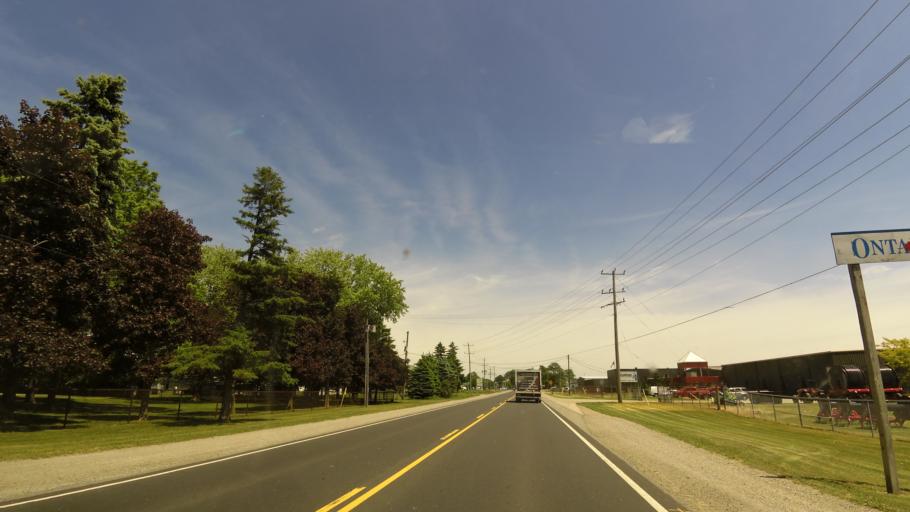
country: CA
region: Ontario
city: Norfolk County
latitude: 42.8440
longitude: -80.6486
